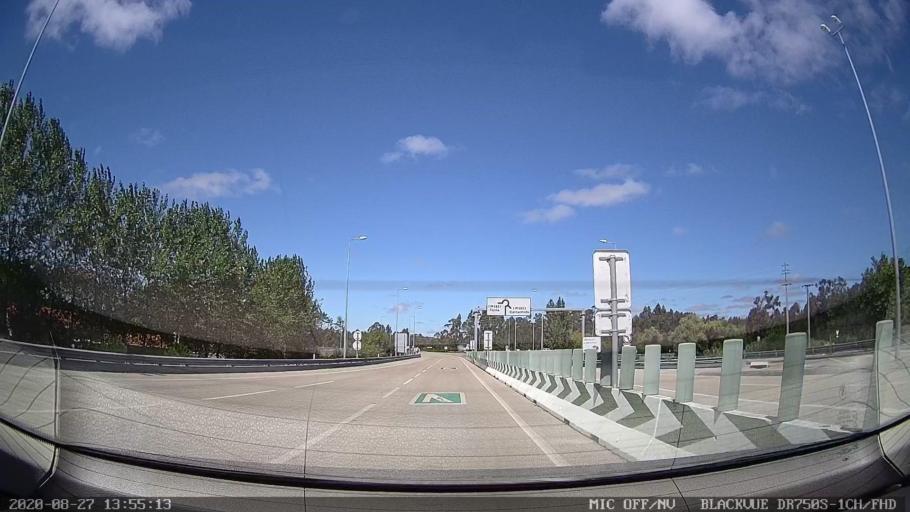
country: PT
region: Coimbra
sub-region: Montemor-O-Velho
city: Arazede
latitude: 40.3297
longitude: -8.7253
